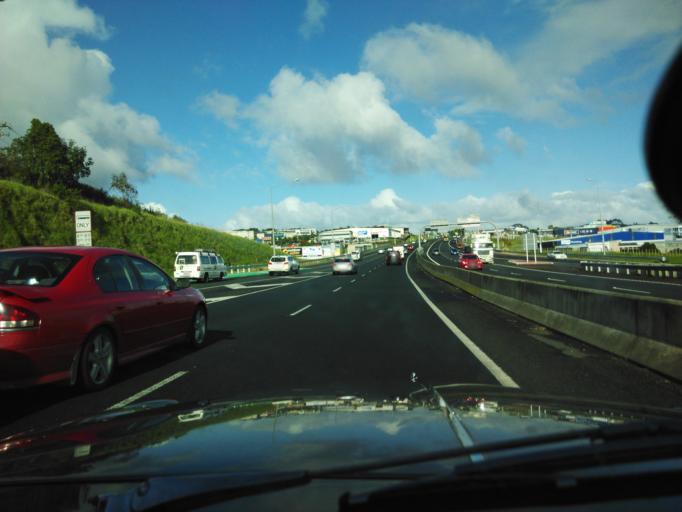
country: NZ
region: Auckland
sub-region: Auckland
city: Rothesay Bay
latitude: -36.7369
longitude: 174.7186
